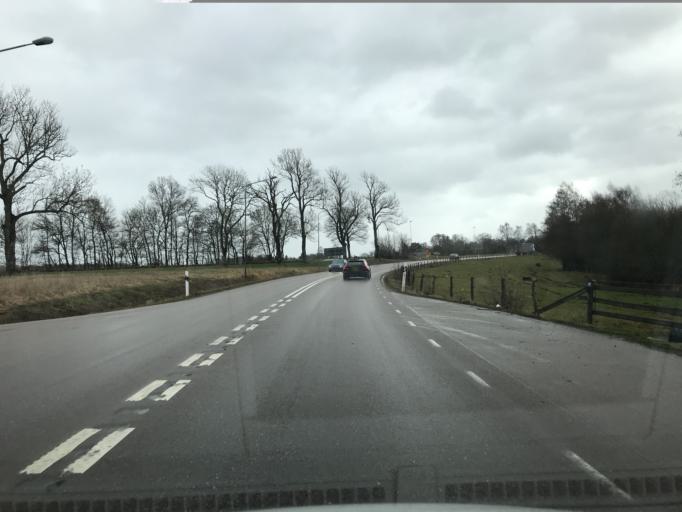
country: SE
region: Skane
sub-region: Klippans Kommun
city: Ljungbyhed
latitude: 56.0862
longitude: 13.2352
